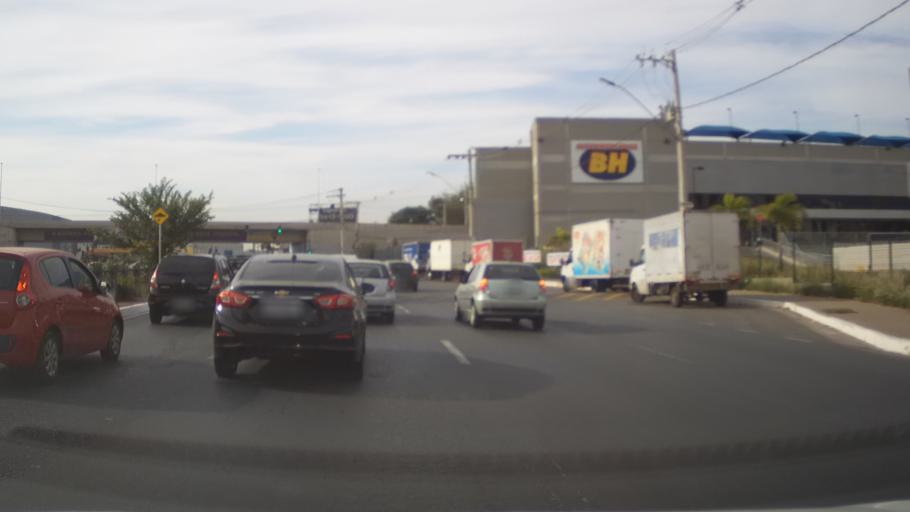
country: BR
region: Minas Gerais
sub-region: Contagem
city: Contagem
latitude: -19.8846
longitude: -44.0392
